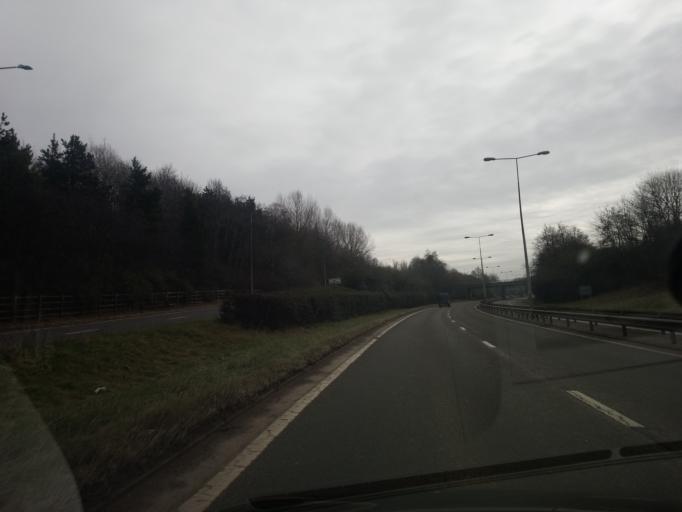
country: GB
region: England
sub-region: Telford and Wrekin
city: Oakengates
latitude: 52.7063
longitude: -2.4609
